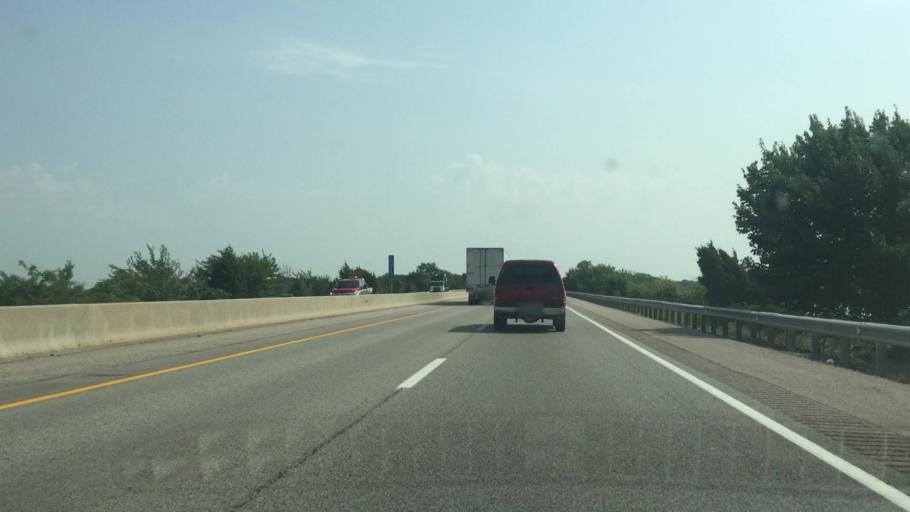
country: US
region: Kansas
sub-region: Butler County
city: El Dorado
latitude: 37.9250
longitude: -96.7860
